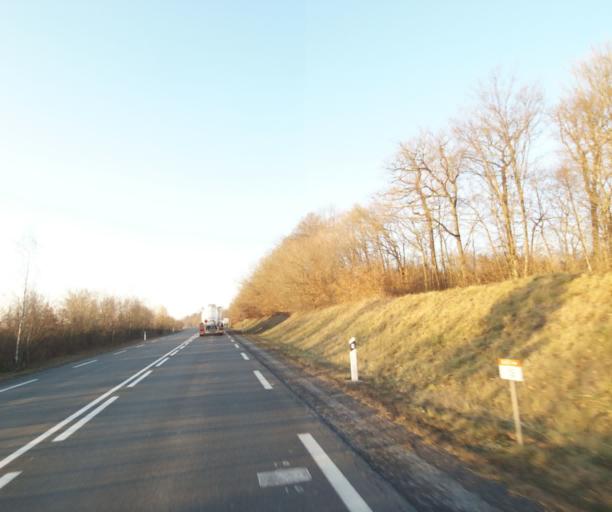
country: FR
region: Champagne-Ardenne
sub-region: Departement de la Haute-Marne
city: Bienville
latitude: 48.5502
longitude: 5.0643
